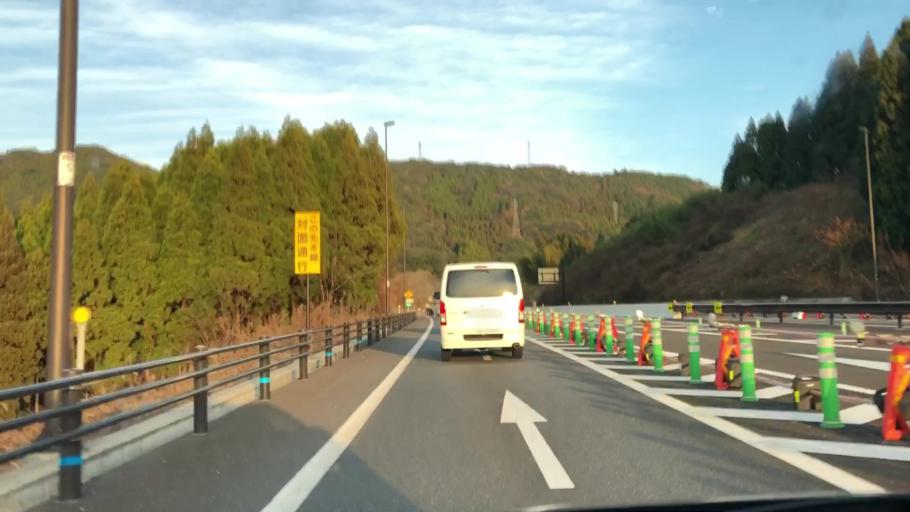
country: JP
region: Kumamoto
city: Minamata
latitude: 32.2432
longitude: 130.4718
